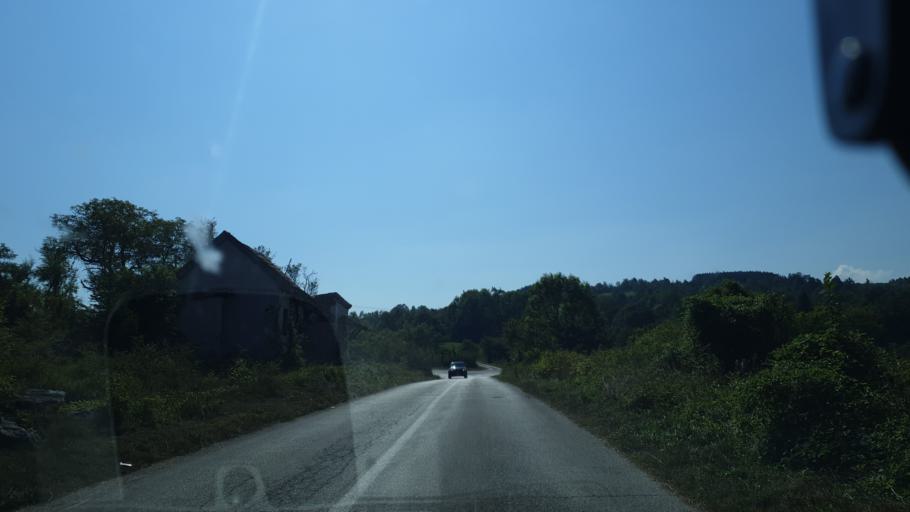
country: RS
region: Central Serbia
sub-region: Zlatiborski Okrug
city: Cajetina
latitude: 43.6997
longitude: 19.8542
